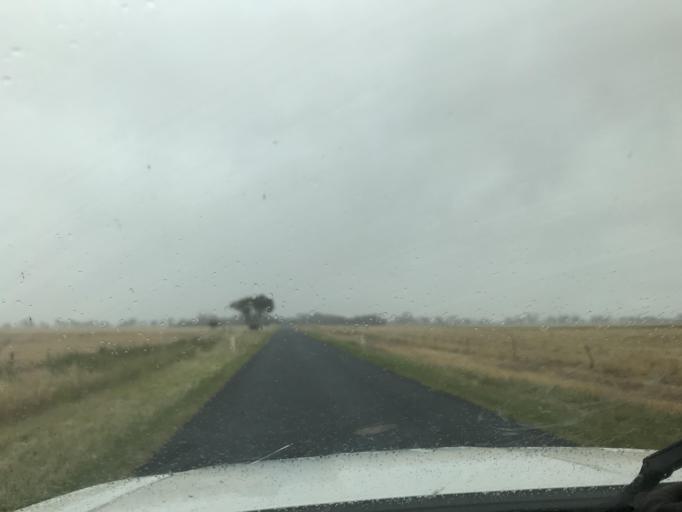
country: AU
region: South Australia
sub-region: Tatiara
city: Bordertown
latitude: -36.3191
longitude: 141.1930
